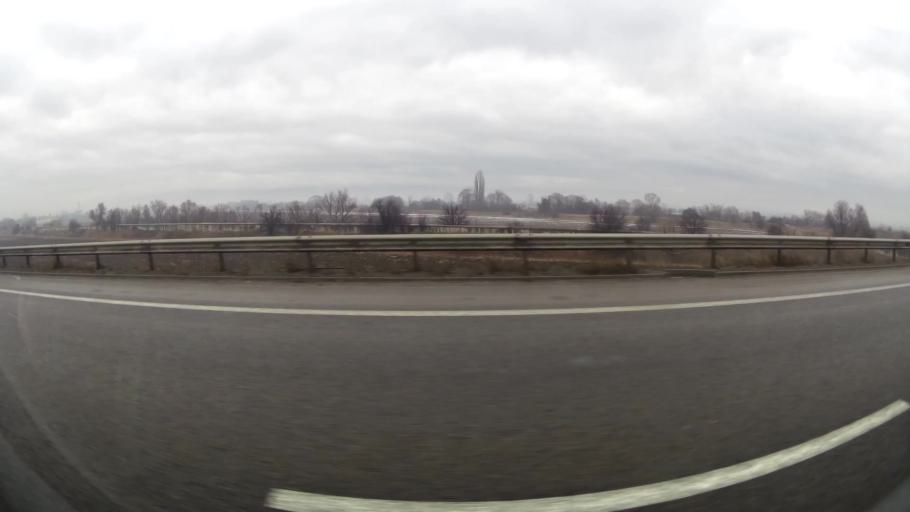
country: BG
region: Sofia-Capital
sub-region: Stolichna Obshtina
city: Sofia
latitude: 42.7423
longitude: 23.3660
